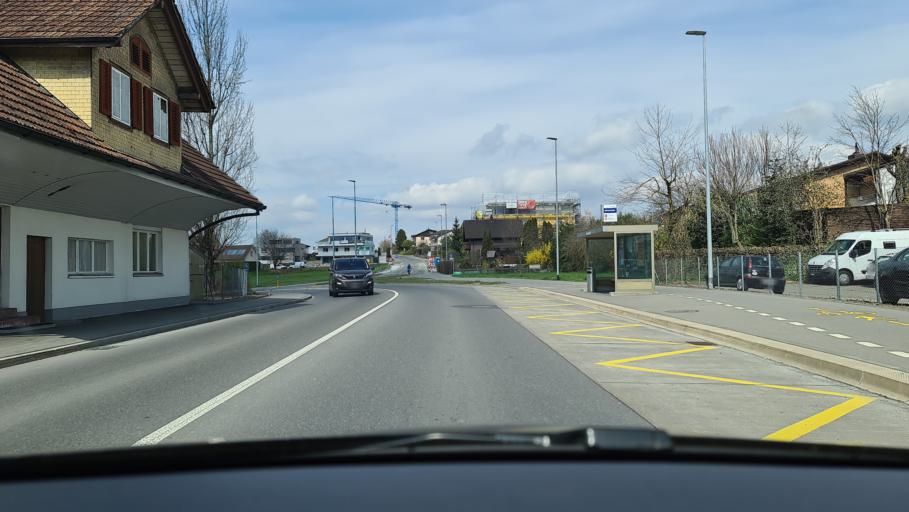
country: CH
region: Zug
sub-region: Zug
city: Steinhausen
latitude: 47.1971
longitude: 8.4799
